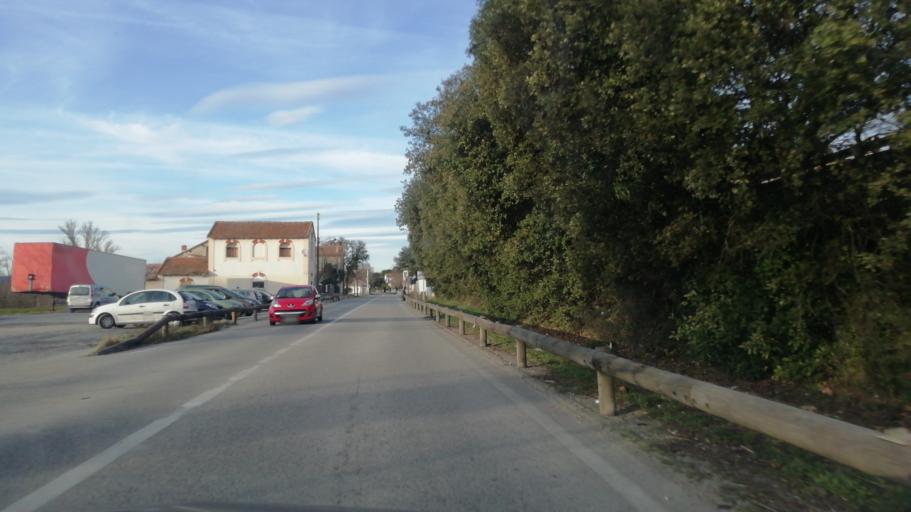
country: FR
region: Languedoc-Roussillon
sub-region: Departement du Gard
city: Quissac
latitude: 43.9020
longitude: 4.0063
